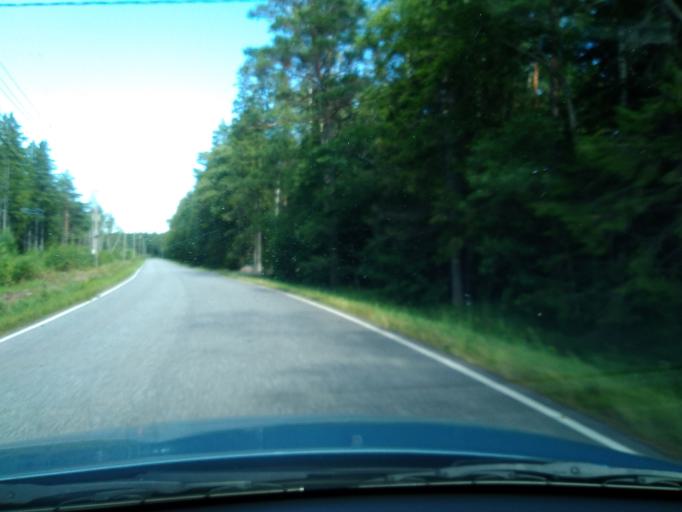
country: FI
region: Uusimaa
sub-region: Raaseporin
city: Hanko
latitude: 59.8364
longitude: 23.1527
